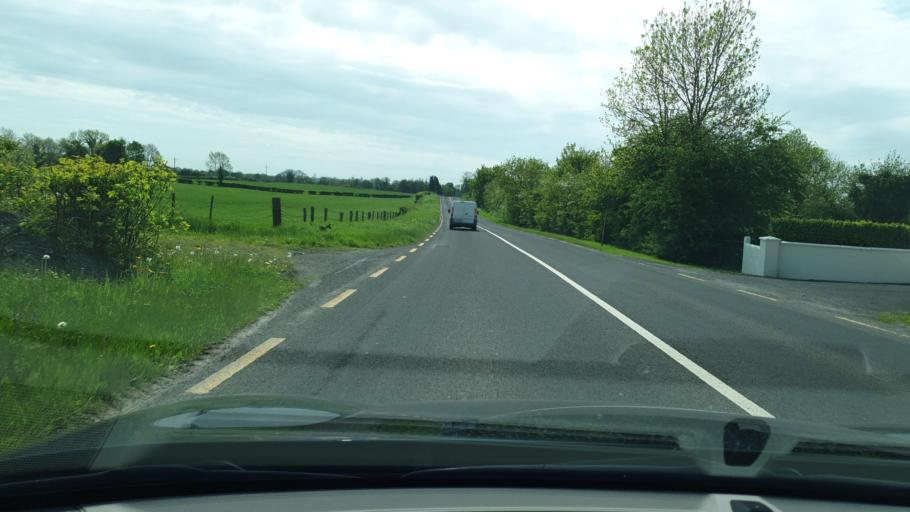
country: IE
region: Leinster
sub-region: An Mhi
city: Navan
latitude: 53.7576
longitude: -6.7240
